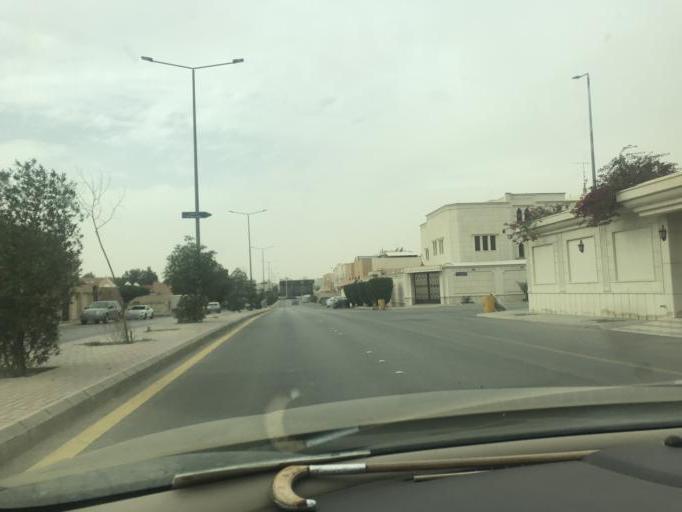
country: SA
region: Ar Riyad
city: Riyadh
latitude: 24.7394
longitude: 46.7534
